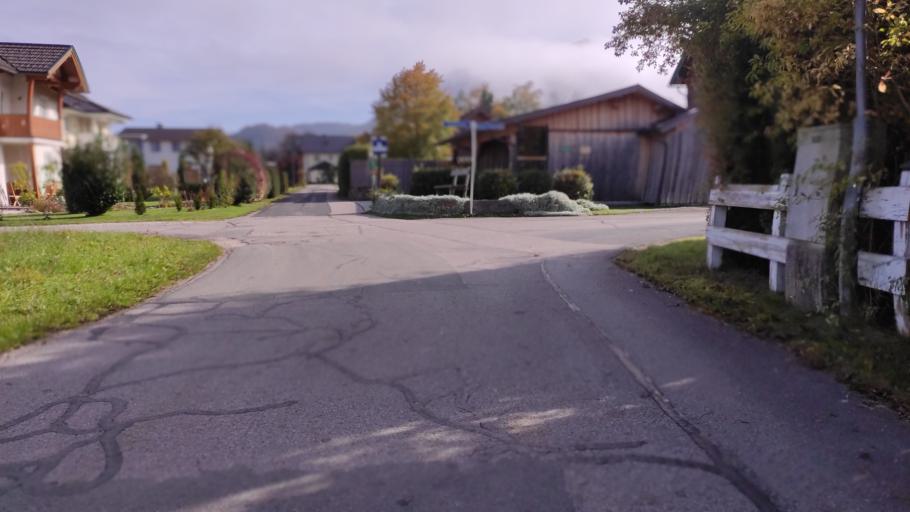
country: AT
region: Salzburg
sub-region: Politischer Bezirk Salzburg-Umgebung
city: Strobl
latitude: 47.7144
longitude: 13.4921
